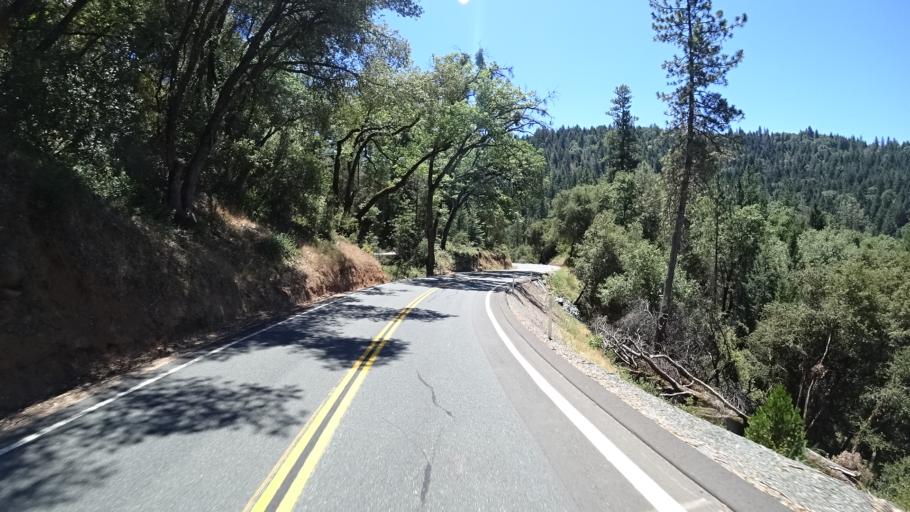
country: US
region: California
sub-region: Amador County
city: Pioneer
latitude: 38.3710
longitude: -120.5533
